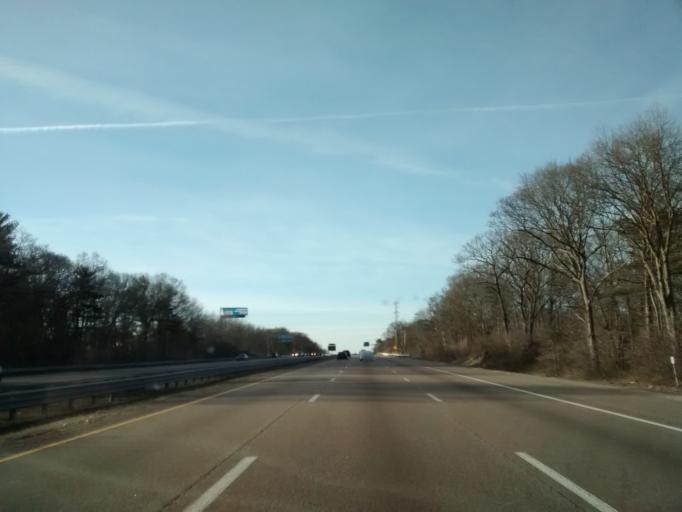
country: US
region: Massachusetts
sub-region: Norfolk County
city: Avon
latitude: 42.1412
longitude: -71.0654
